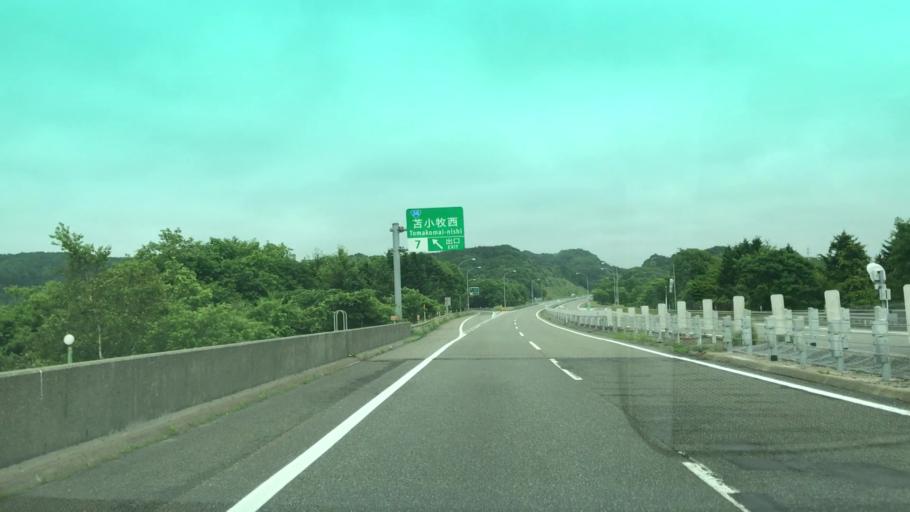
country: JP
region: Hokkaido
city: Tomakomai
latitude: 42.6301
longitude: 141.4863
